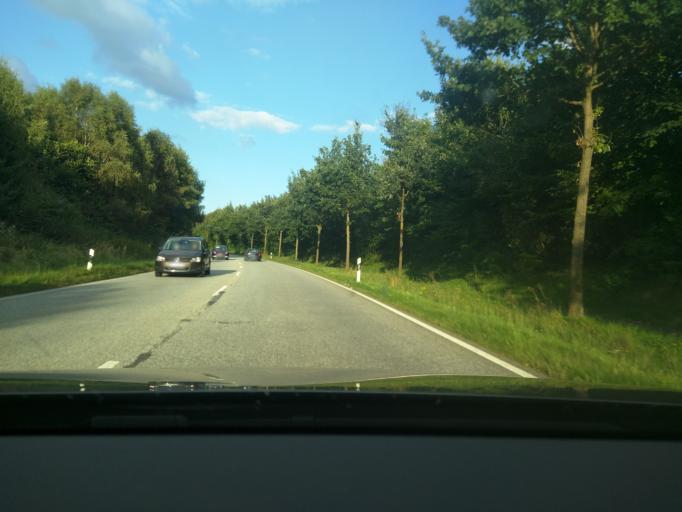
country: DE
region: Schleswig-Holstein
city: Schwarzenbek
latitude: 53.5123
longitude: 10.4672
